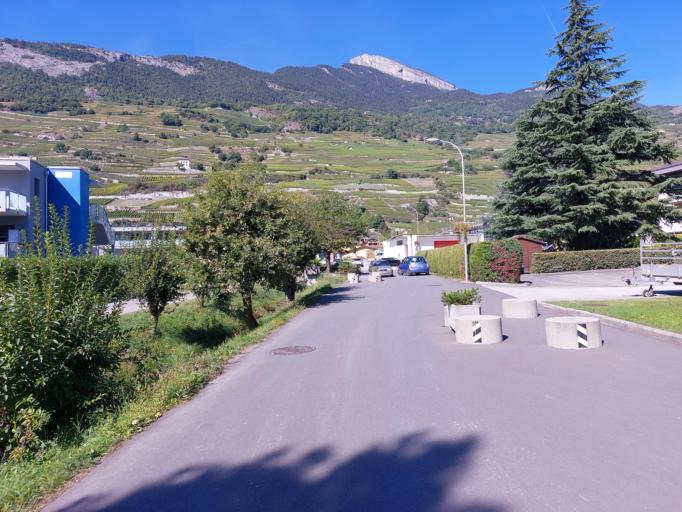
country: CH
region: Valais
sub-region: Conthey District
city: Vetroz
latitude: 46.2236
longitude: 7.2789
